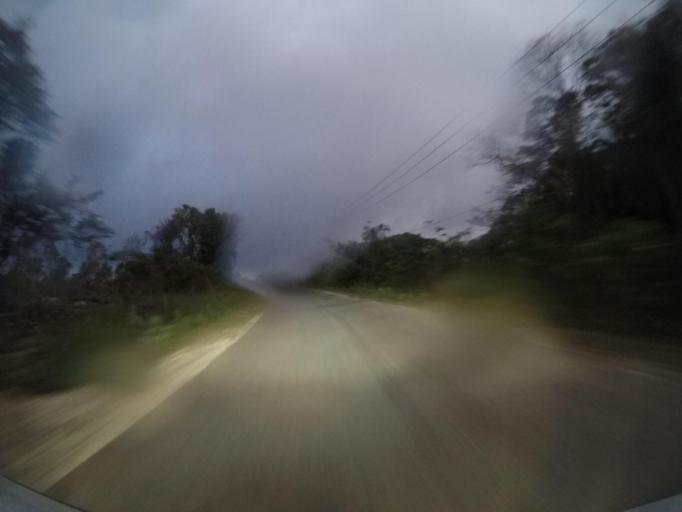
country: TL
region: Lautem
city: Lospalos
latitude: -8.4112
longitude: 126.9983
